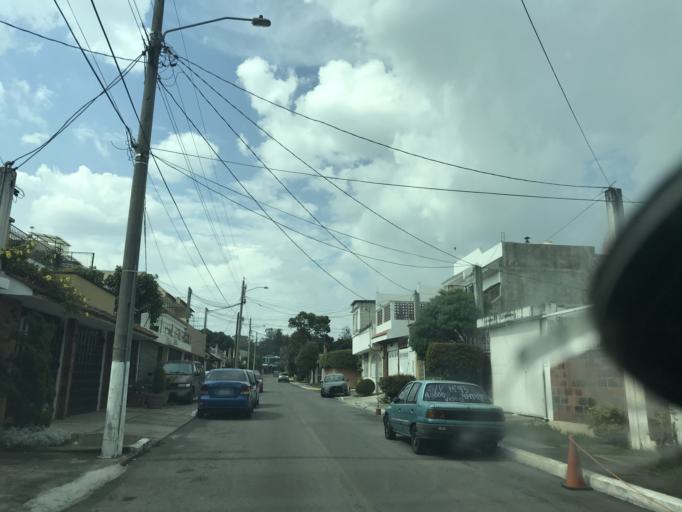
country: GT
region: Guatemala
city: Santa Catarina Pinula
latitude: 14.5807
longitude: -90.5527
